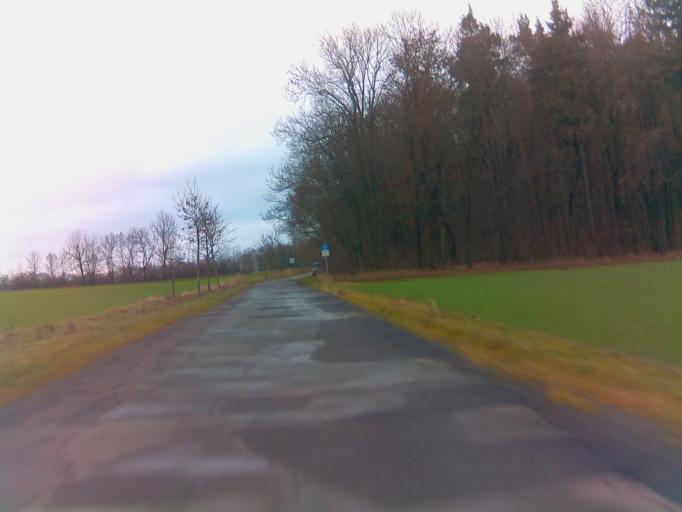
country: DE
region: Thuringia
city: Nauendorf
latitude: 50.9104
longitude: 11.1912
